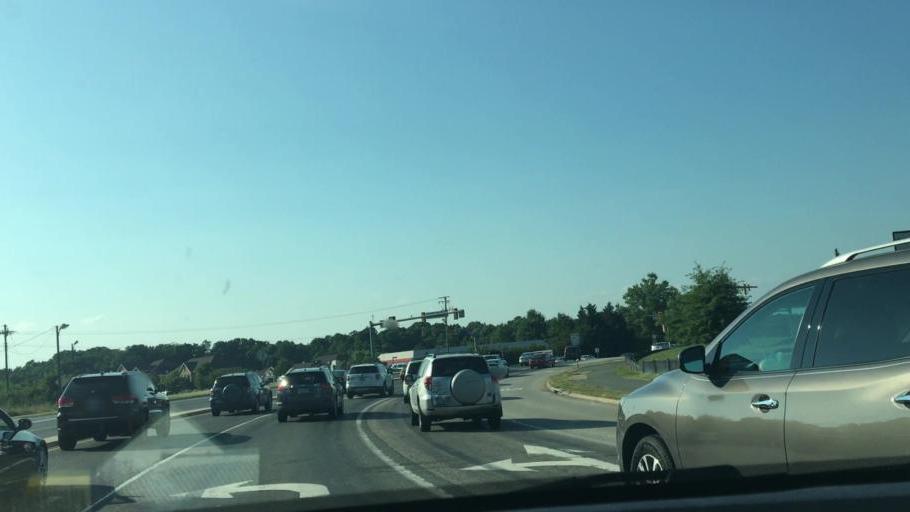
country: US
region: Virginia
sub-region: Prince William County
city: Lake Ridge
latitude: 38.6719
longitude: -77.3361
